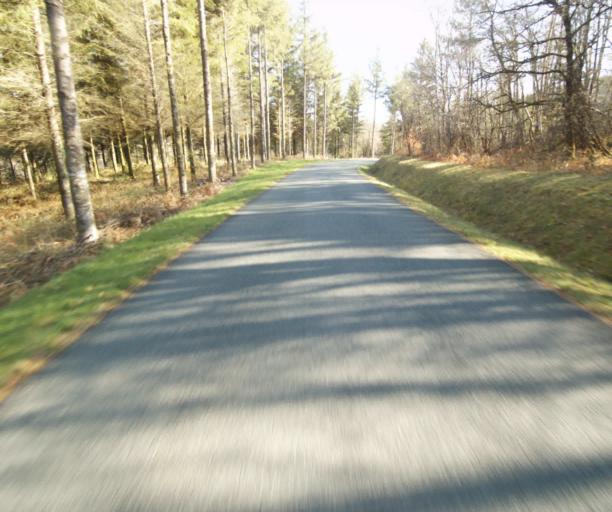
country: FR
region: Limousin
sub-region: Departement de la Correze
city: Correze
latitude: 45.3089
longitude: 1.8815
